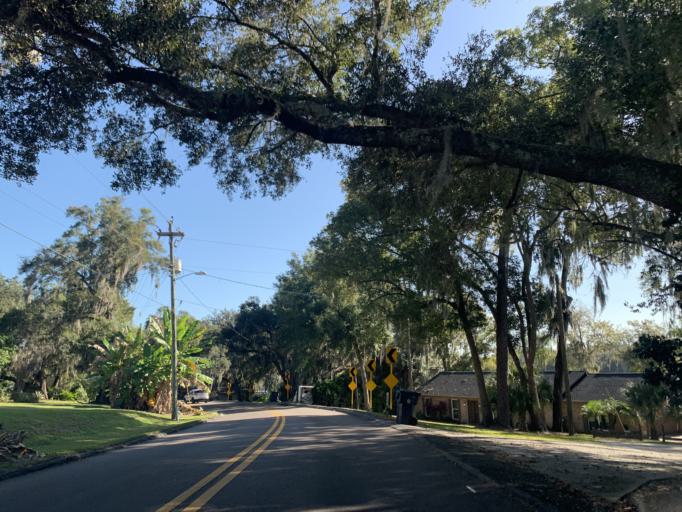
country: US
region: Florida
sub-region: Hillsborough County
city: Temple Terrace
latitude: 28.0216
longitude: -82.4110
